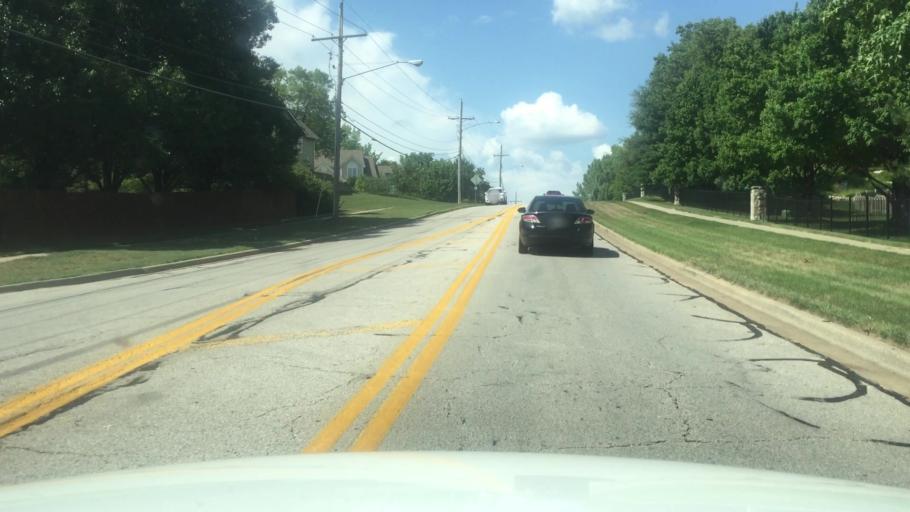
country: US
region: Kansas
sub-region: Johnson County
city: Lenexa
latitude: 38.9959
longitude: -94.7423
